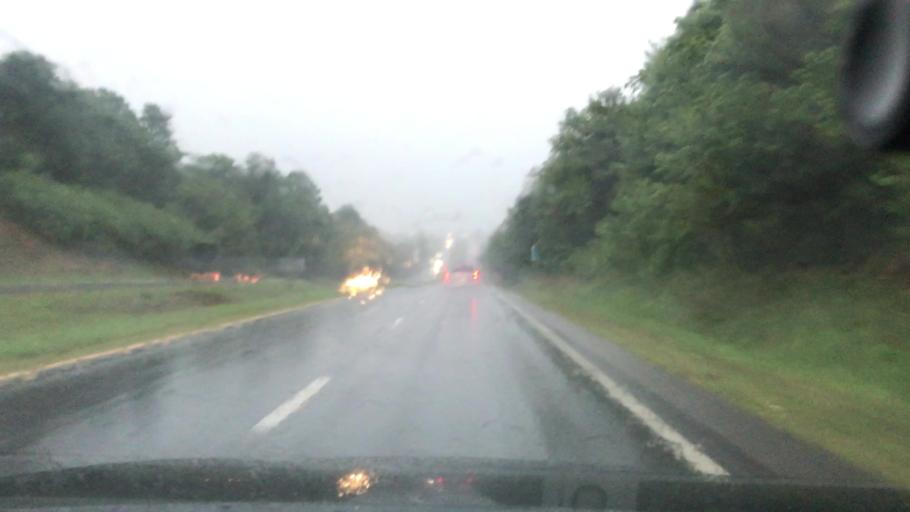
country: US
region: Virginia
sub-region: Giles County
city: Pearisburg
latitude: 37.3363
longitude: -80.7058
